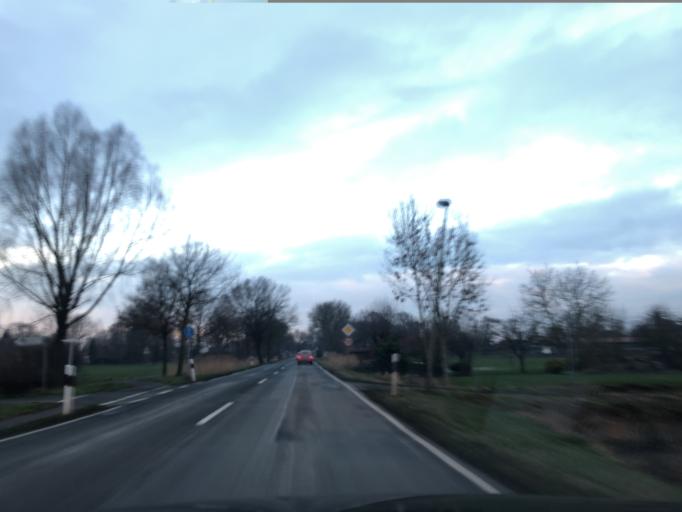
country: DE
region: Lower Saxony
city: Lemwerder
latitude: 53.1266
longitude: 8.6291
